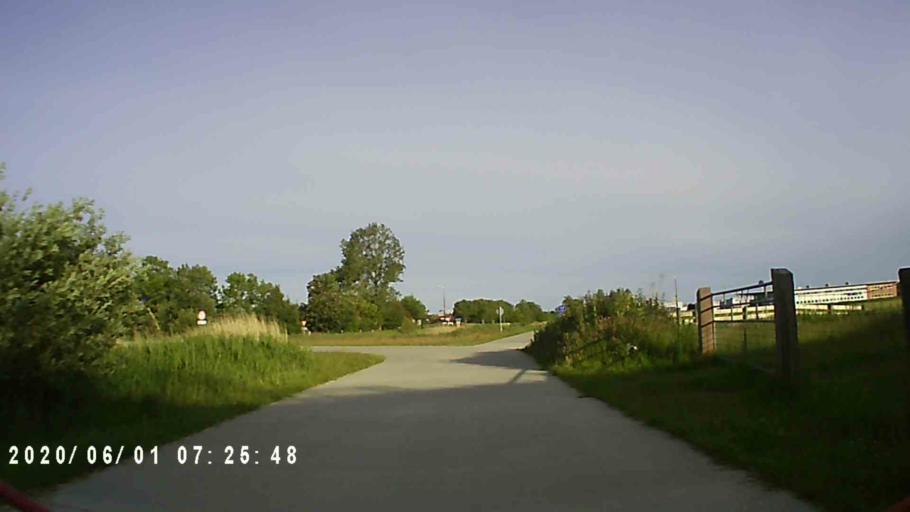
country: NL
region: Friesland
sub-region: Gemeente Dantumadiel
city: Walterswald
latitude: 53.3177
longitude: 6.0212
